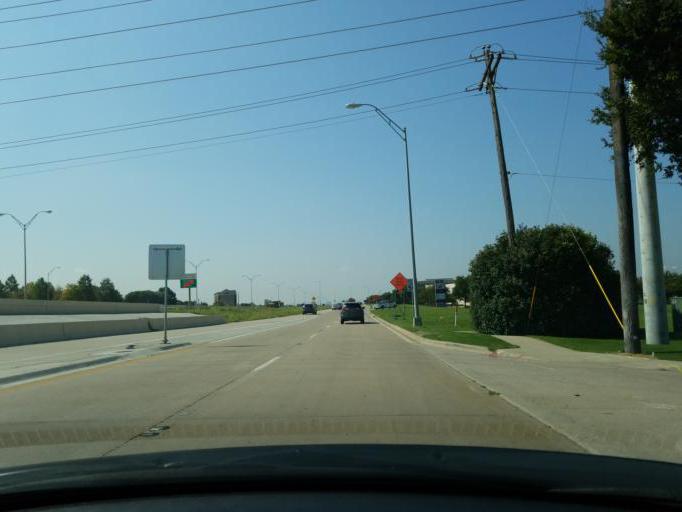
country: US
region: Texas
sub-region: Collin County
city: Allen
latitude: 33.0984
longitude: -96.6794
